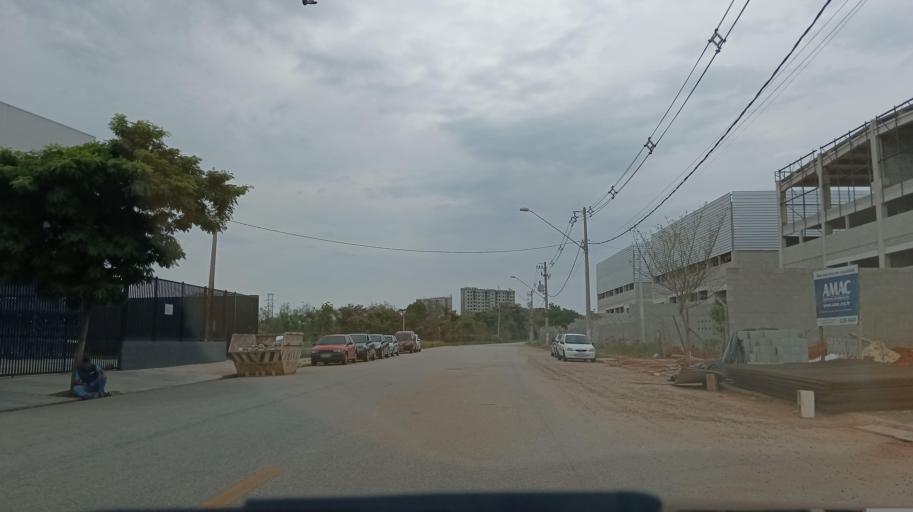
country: BR
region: Sao Paulo
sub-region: Sorocaba
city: Sorocaba
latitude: -23.4571
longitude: -47.4585
